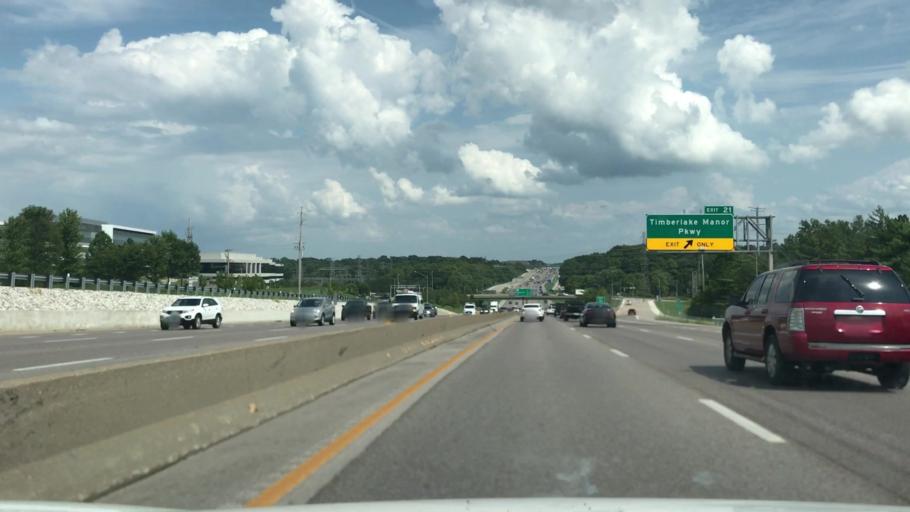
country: US
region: Missouri
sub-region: Saint Louis County
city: Chesterfield
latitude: 38.6478
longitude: -90.5359
